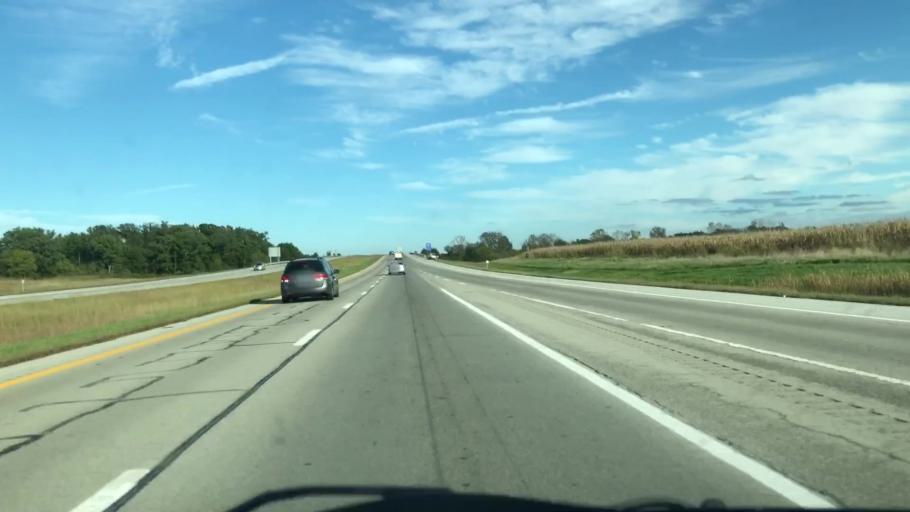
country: US
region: Ohio
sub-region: Allen County
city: Lima
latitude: 40.8237
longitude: -84.0889
